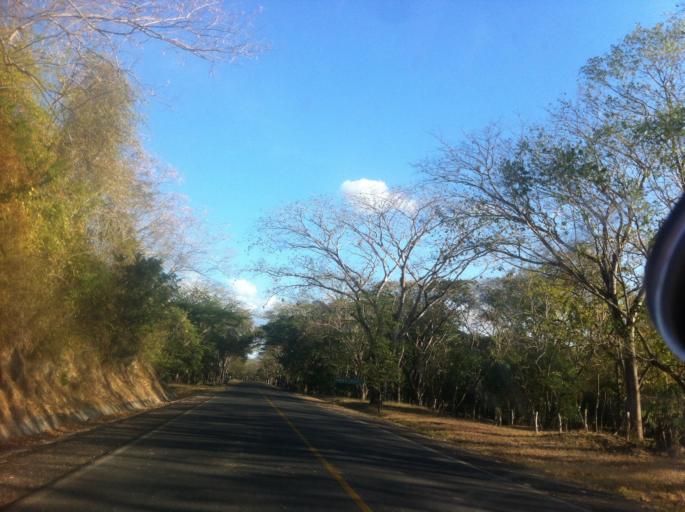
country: NI
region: Rio San Juan
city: Morrito
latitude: 11.7227
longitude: -84.9650
